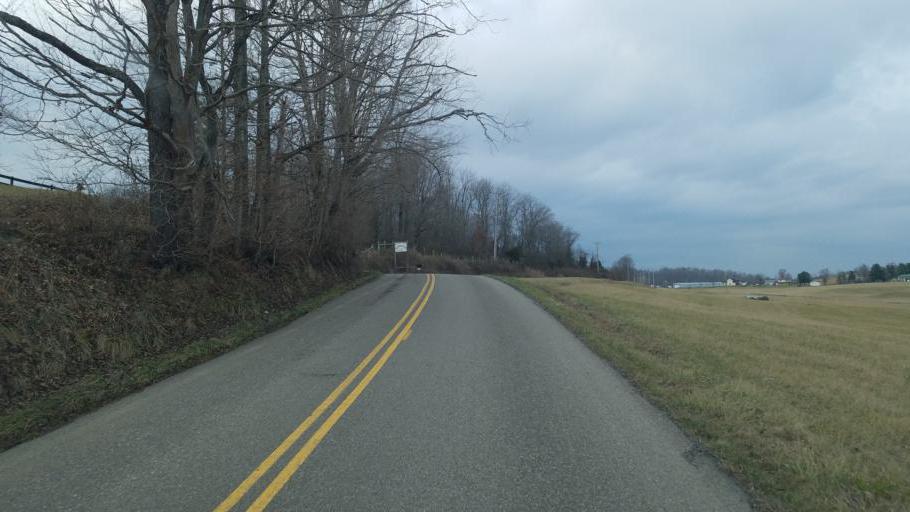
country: US
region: Ohio
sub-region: Gallia County
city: Gallipolis
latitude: 38.7680
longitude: -82.3770
